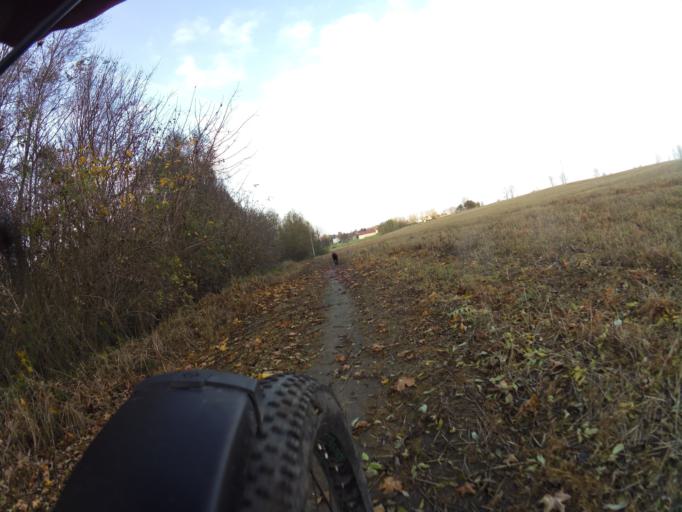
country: PL
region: Pomeranian Voivodeship
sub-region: Powiat pucki
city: Krokowa
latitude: 54.7732
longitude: 18.1709
